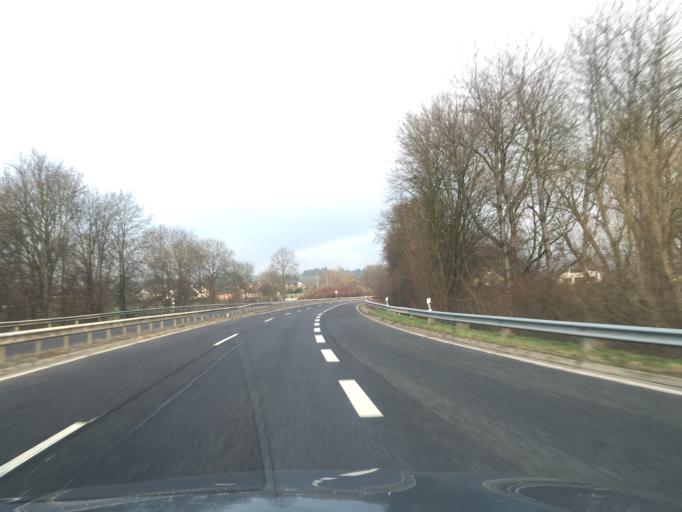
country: DE
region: Rheinland-Pfalz
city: Andernach
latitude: 50.4268
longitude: 7.3888
